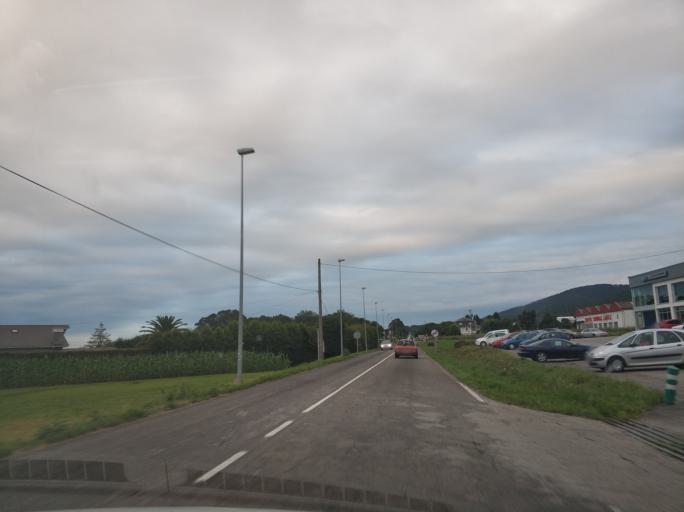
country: ES
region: Asturias
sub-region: Province of Asturias
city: Navia
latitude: 43.5345
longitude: -6.5225
